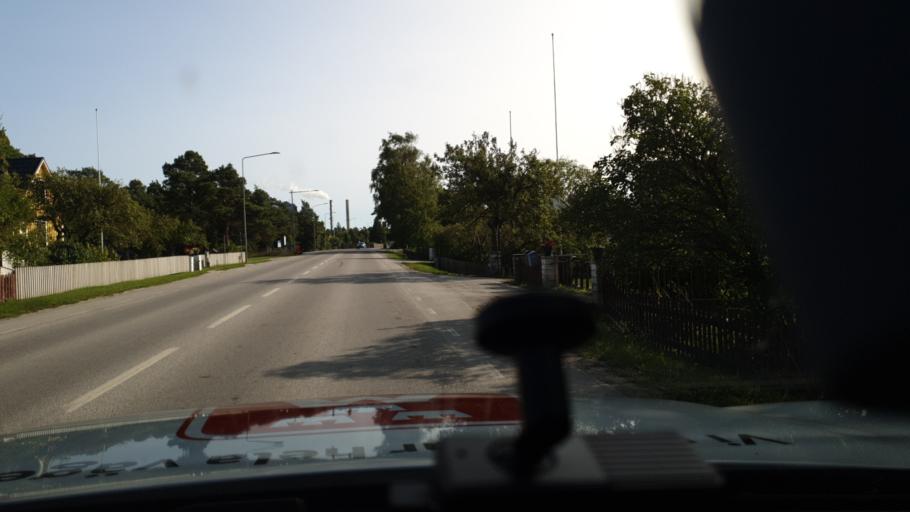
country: SE
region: Gotland
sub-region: Gotland
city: Slite
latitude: 57.7222
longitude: 18.7891
